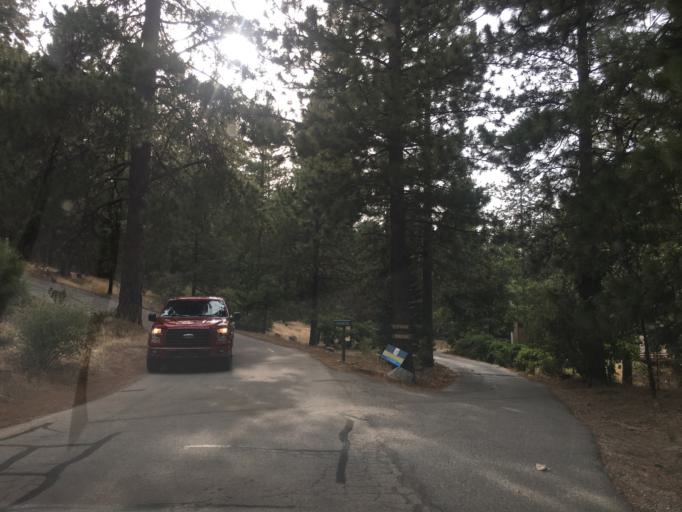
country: US
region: California
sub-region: San Bernardino County
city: Crestline
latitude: 34.2517
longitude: -117.2766
